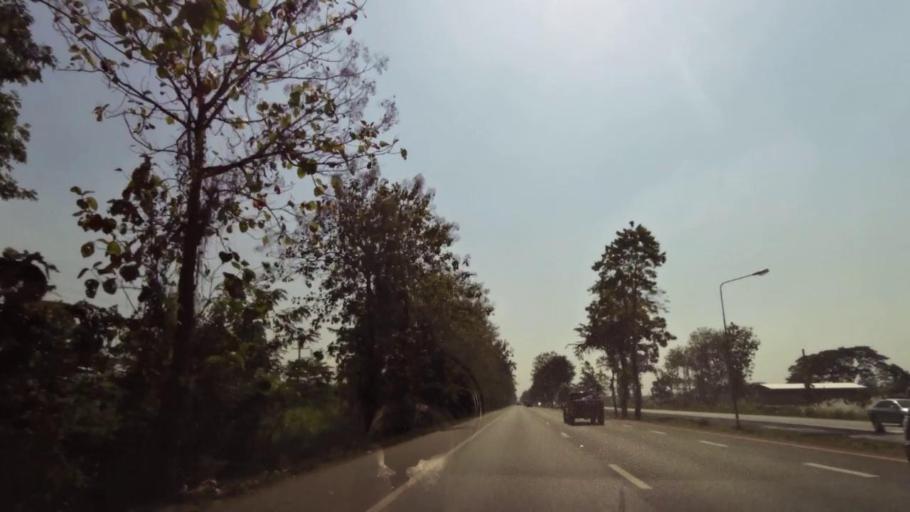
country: TH
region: Phichit
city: Bueng Na Rang
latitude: 16.0893
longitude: 100.1251
